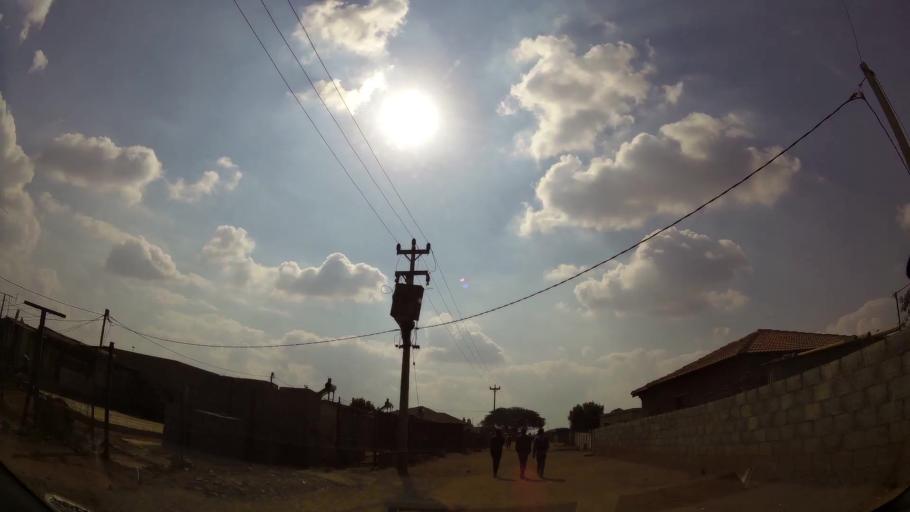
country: ZA
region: Gauteng
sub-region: Ekurhuleni Metropolitan Municipality
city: Springs
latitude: -26.1226
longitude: 28.4794
